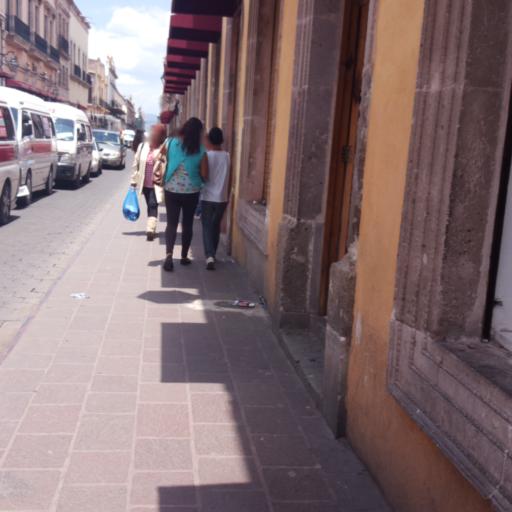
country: MX
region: Michoacan
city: Morelia
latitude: 19.7019
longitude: -101.1906
